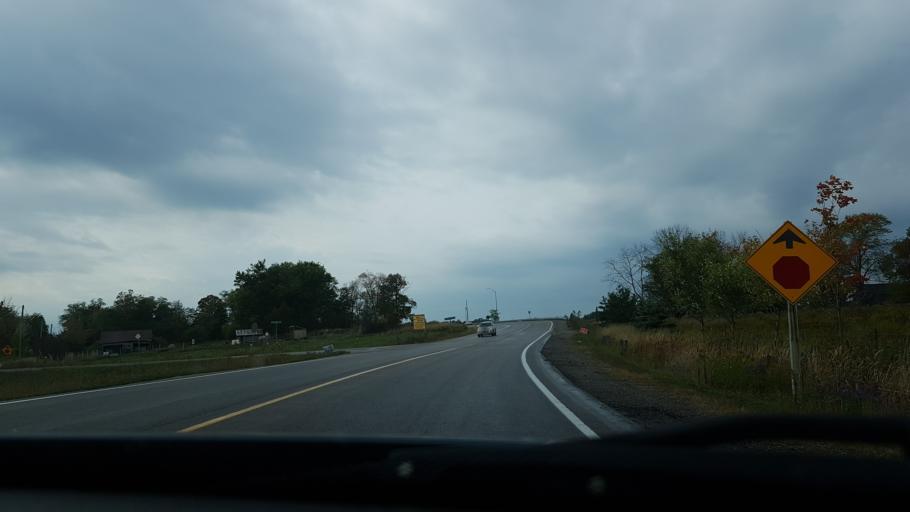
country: CA
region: Ontario
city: Omemee
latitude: 44.4861
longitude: -78.7565
